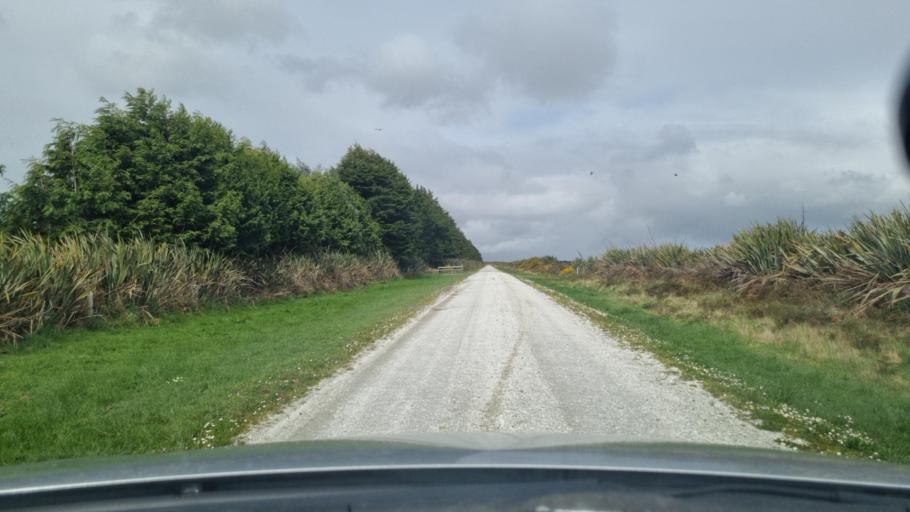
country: NZ
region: Southland
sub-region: Invercargill City
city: Bluff
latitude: -46.5142
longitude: 168.3568
